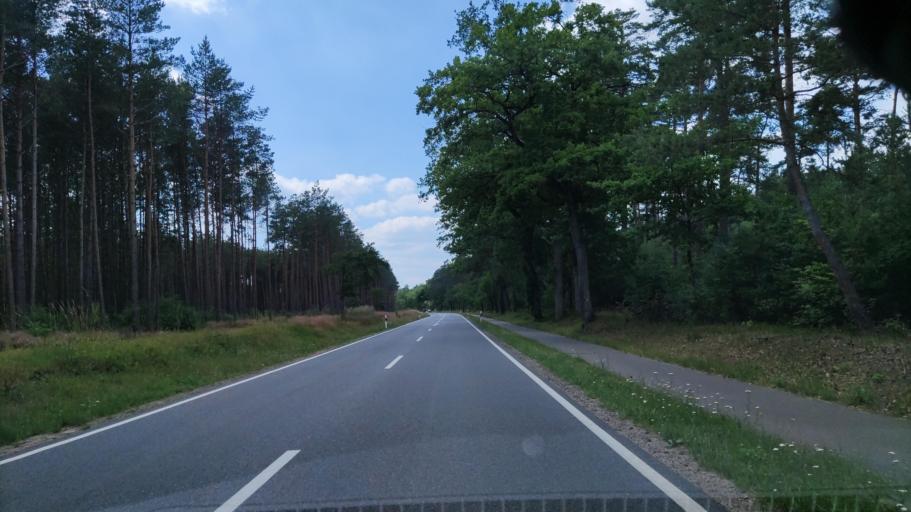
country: DE
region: Mecklenburg-Vorpommern
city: Lubtheen
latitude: 53.3212
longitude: 11.1223
